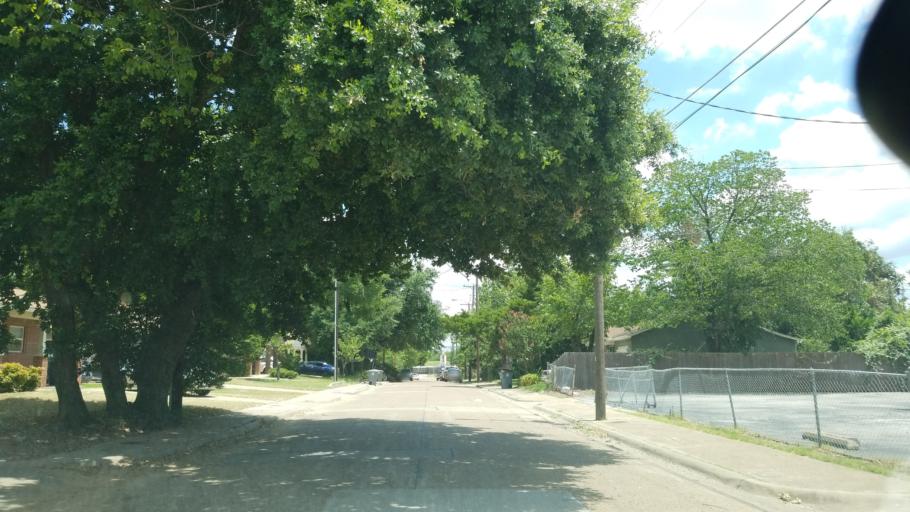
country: US
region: Texas
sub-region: Dallas County
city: Dallas
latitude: 32.7363
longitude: -96.7532
